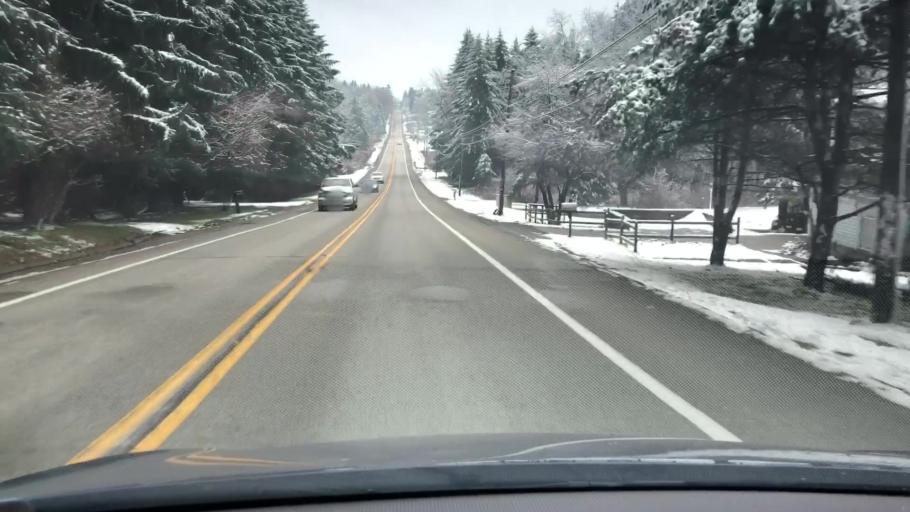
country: US
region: Pennsylvania
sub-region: Fayette County
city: Hopwood
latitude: 39.8262
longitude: -79.5953
